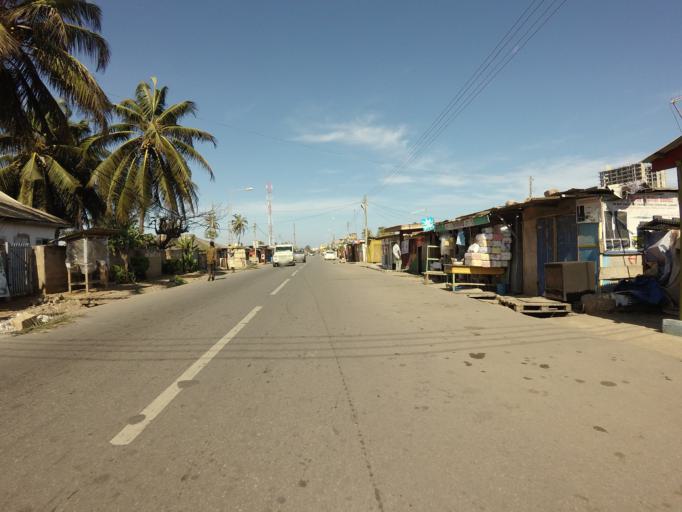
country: GH
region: Greater Accra
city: Accra
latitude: 5.5621
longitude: -0.1498
